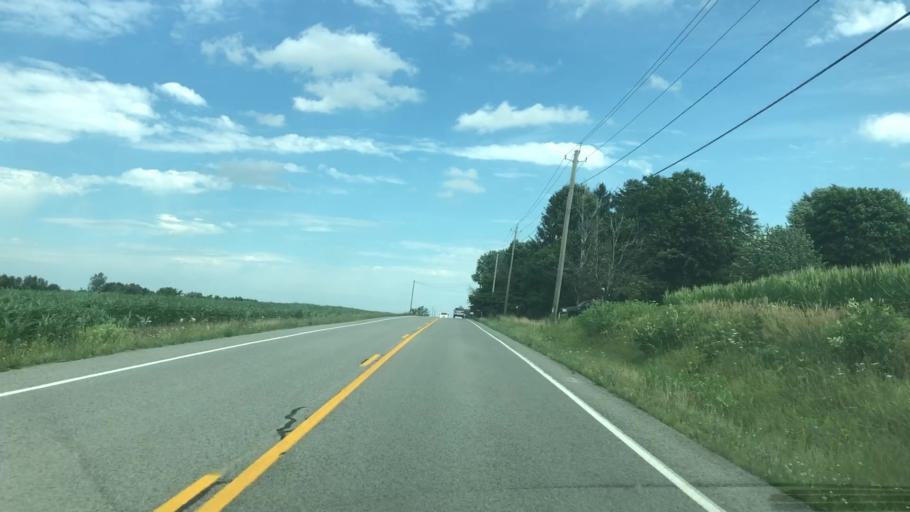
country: US
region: New York
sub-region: Wayne County
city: Macedon
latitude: 43.1013
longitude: -77.3521
